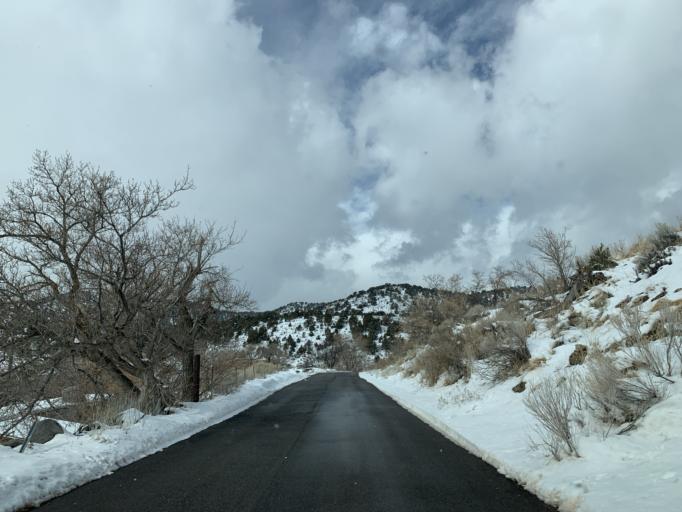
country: US
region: Utah
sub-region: Utah County
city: Genola
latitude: 39.9568
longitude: -112.1209
